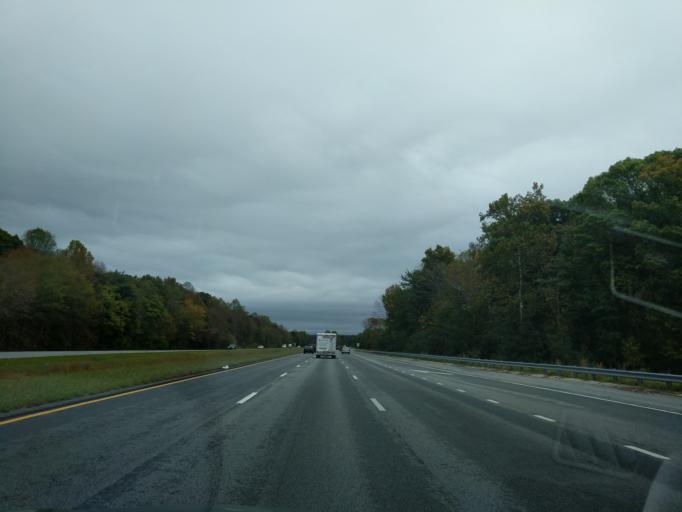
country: US
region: North Carolina
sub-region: Randolph County
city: Trinity
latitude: 35.8664
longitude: -80.0315
